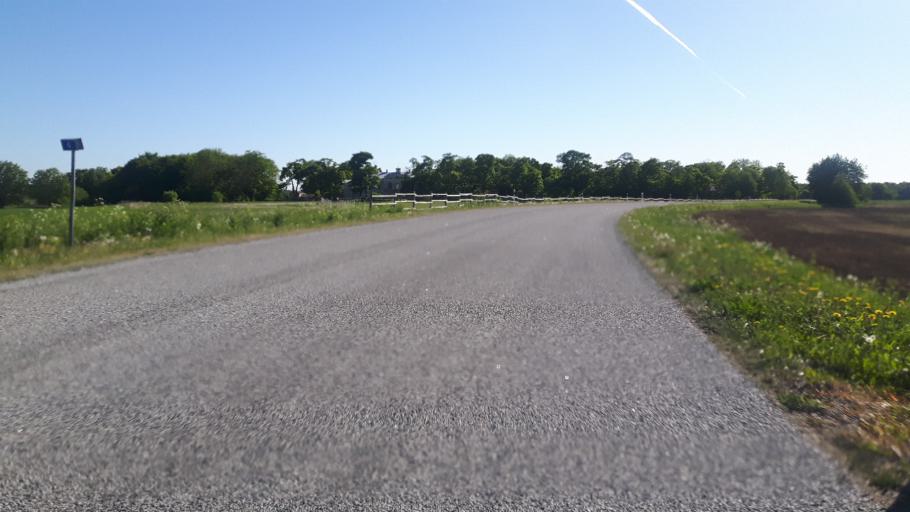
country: EE
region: Ida-Virumaa
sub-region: Kohtla-Jaerve linn
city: Kohtla-Jarve
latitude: 59.4399
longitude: 27.3032
